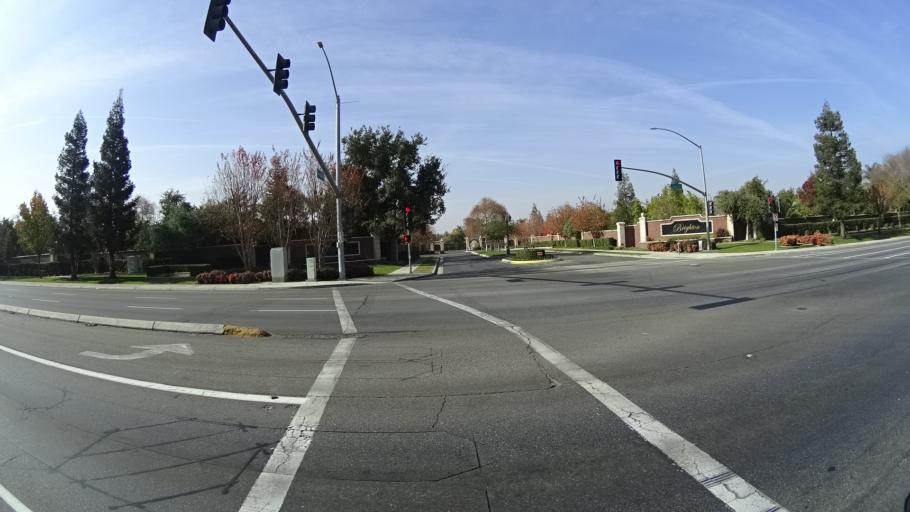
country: US
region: California
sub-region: Kern County
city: Greenacres
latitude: 35.3591
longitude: -119.1160
